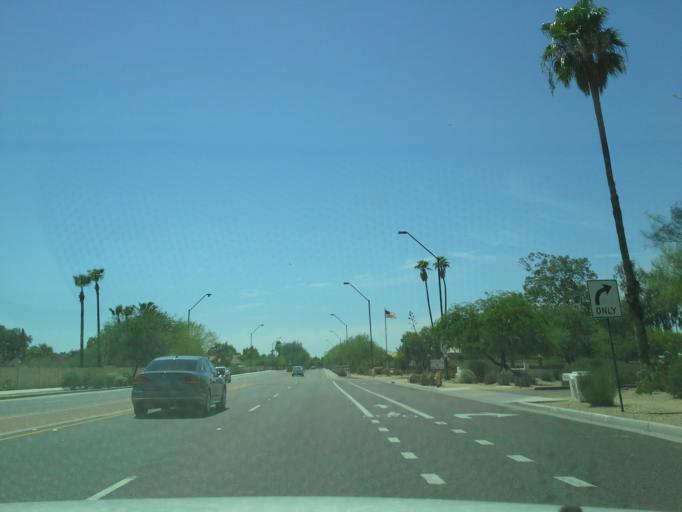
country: US
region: Arizona
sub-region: Maricopa County
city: Scottsdale
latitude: 33.5971
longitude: -111.8795
